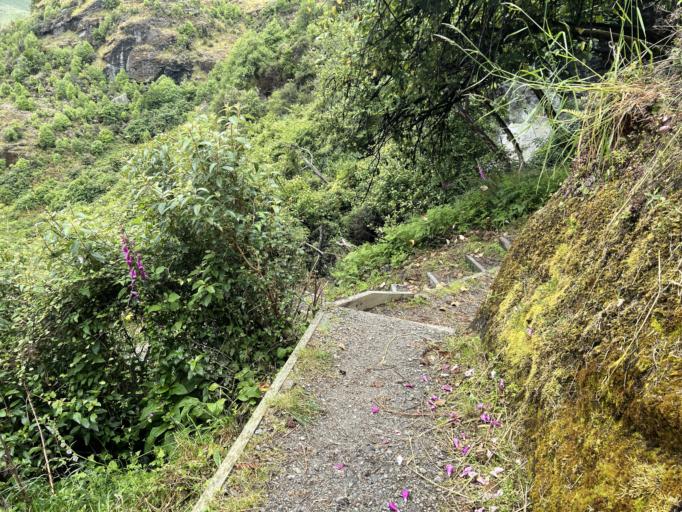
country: NZ
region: Otago
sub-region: Queenstown-Lakes District
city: Wanaka
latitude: -44.6459
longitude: 168.9632
